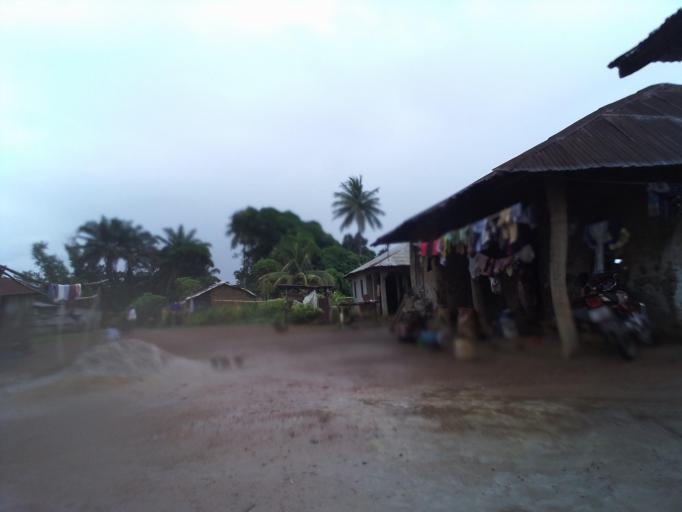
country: SL
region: Eastern Province
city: Kenema
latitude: 7.8811
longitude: -11.1564
